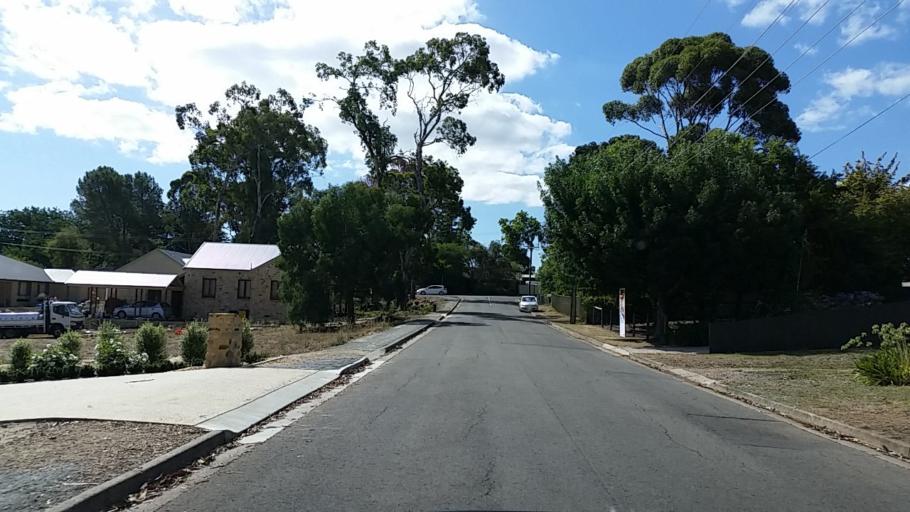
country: AU
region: South Australia
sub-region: Mount Barker
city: Hahndorf
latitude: -35.0272
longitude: 138.8155
